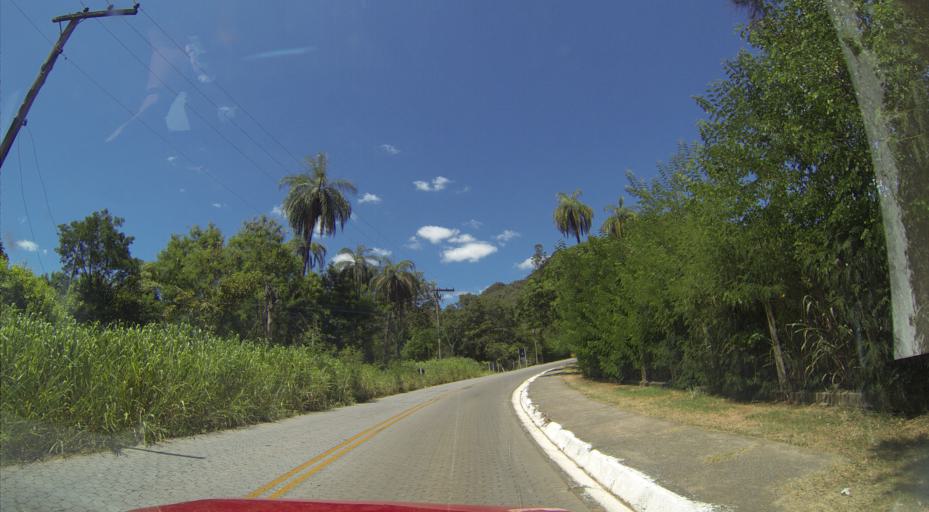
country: BR
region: Minas Gerais
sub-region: Conceicao Do Mato Dentro
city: Conceicao do Mato Dentro
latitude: -19.3168
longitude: -43.6087
